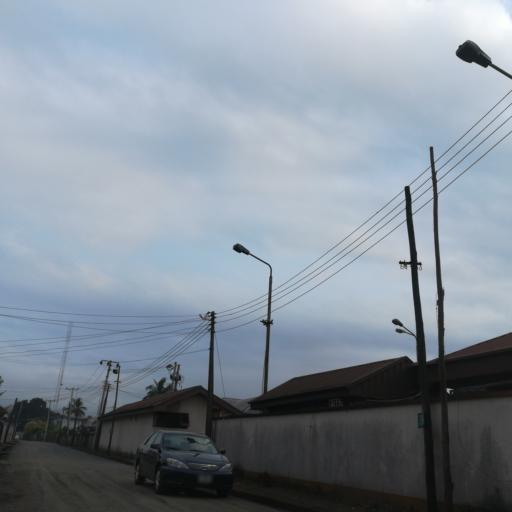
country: NG
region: Rivers
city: Port Harcourt
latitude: 4.8423
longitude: 7.0487
